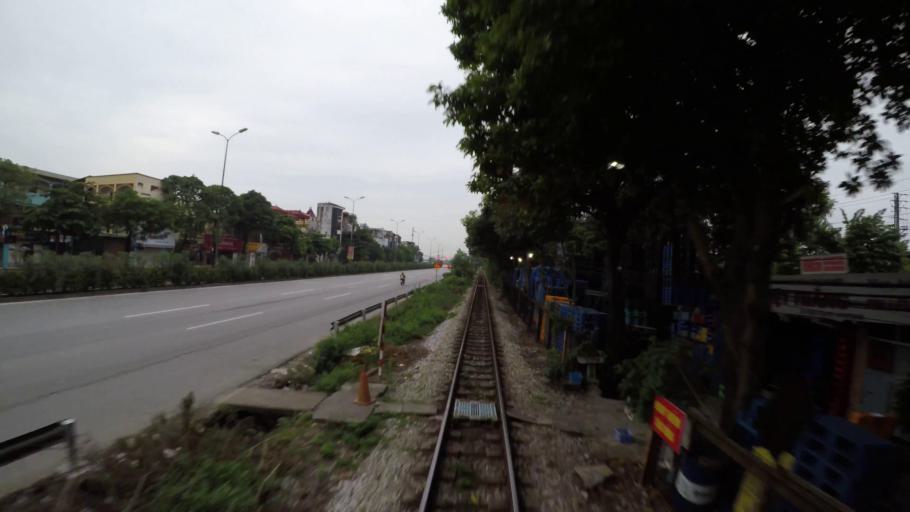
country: VN
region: Hung Yen
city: Nhu Quynh
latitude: 21.0027
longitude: 105.9634
